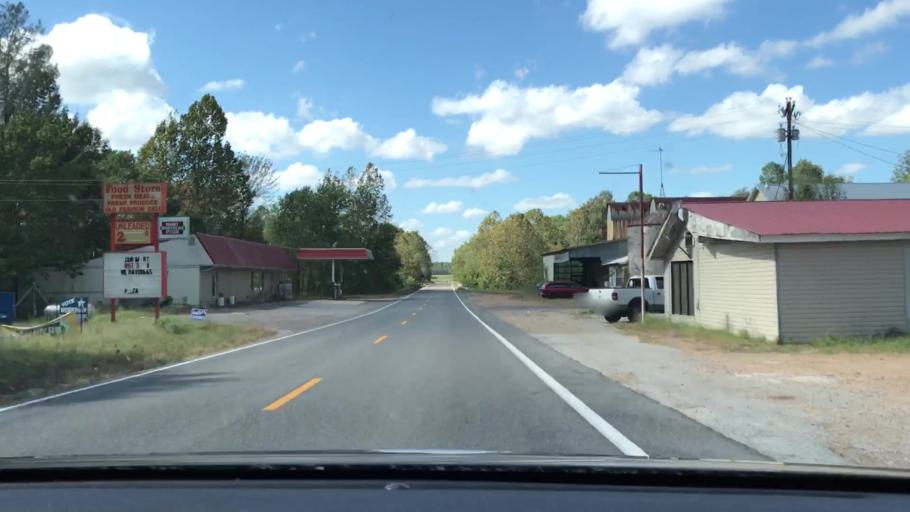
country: US
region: Kentucky
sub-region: McCracken County
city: Reidland
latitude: 36.8857
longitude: -88.5460
